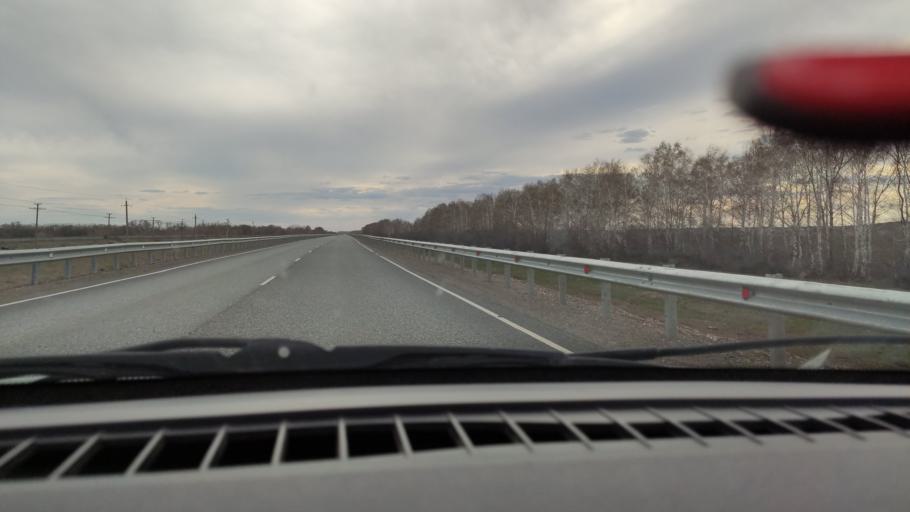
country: RU
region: Bashkortostan
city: Mayachnyy
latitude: 52.4085
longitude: 55.7386
